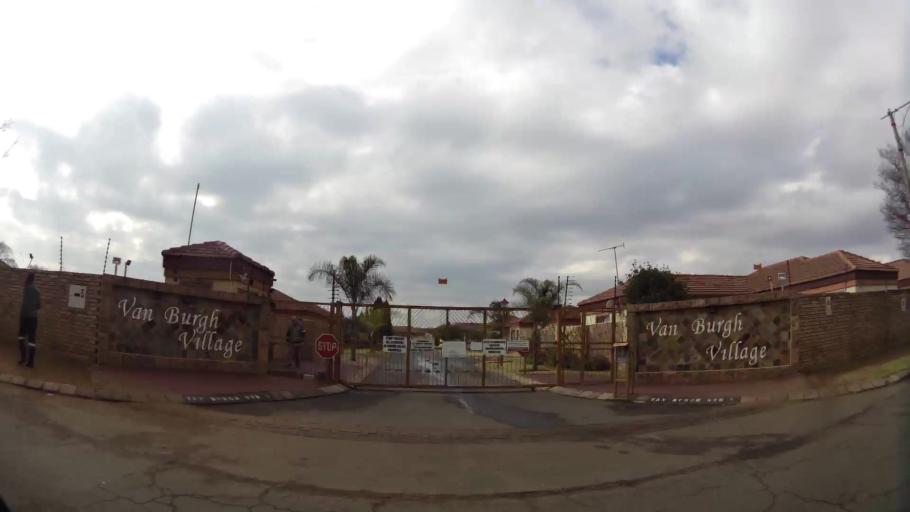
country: ZA
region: Gauteng
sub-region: Sedibeng District Municipality
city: Vanderbijlpark
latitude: -26.6915
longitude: 27.8389
